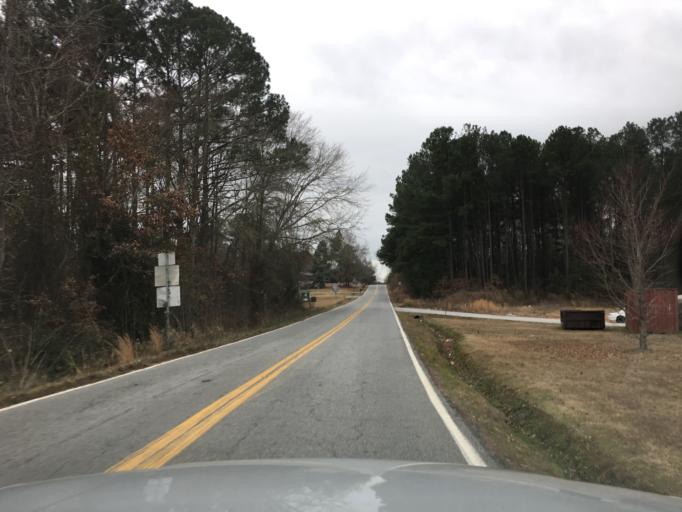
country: US
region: South Carolina
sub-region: Greenwood County
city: Greenwood
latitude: 34.2333
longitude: -82.1035
